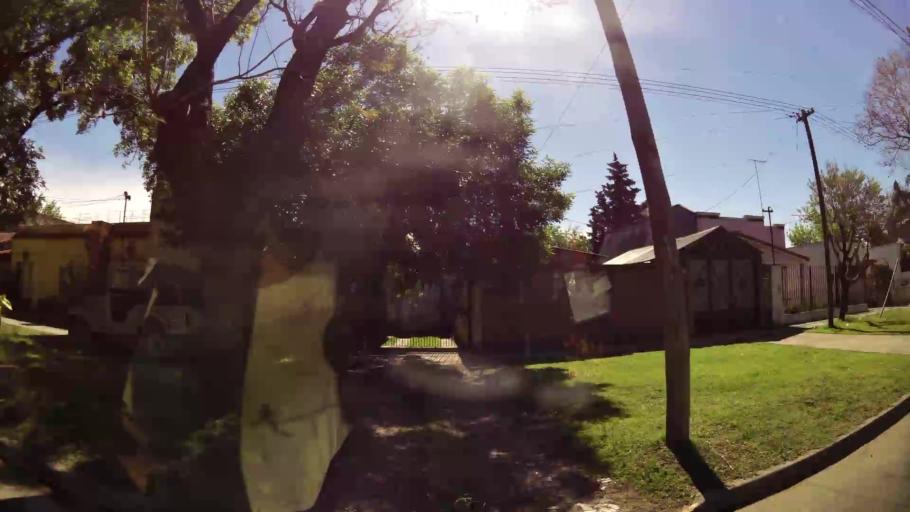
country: AR
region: Buenos Aires
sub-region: Partido de Almirante Brown
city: Adrogue
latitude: -34.7968
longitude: -58.3642
